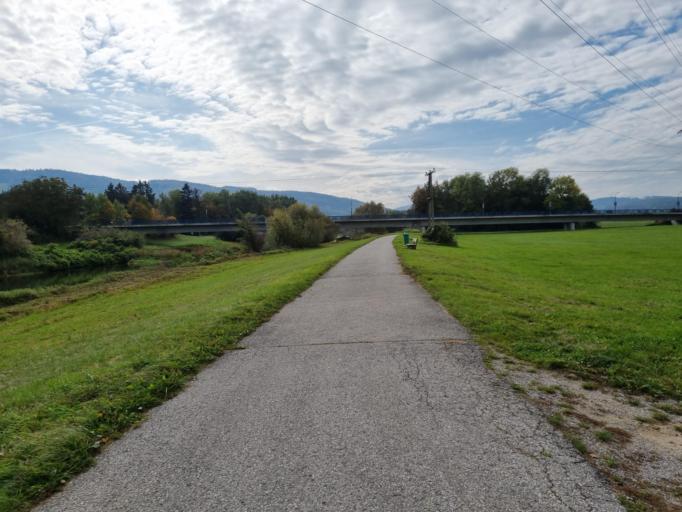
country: AT
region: Lower Austria
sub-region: Politischer Bezirk Sankt Polten
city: Wilhelmsburg
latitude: 48.1329
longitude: 15.6311
